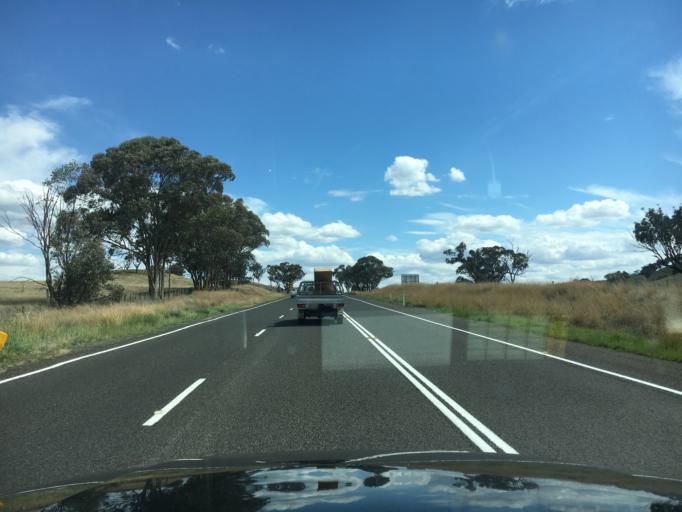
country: AU
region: New South Wales
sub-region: Liverpool Plains
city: Quirindi
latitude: -31.4986
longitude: 150.8647
